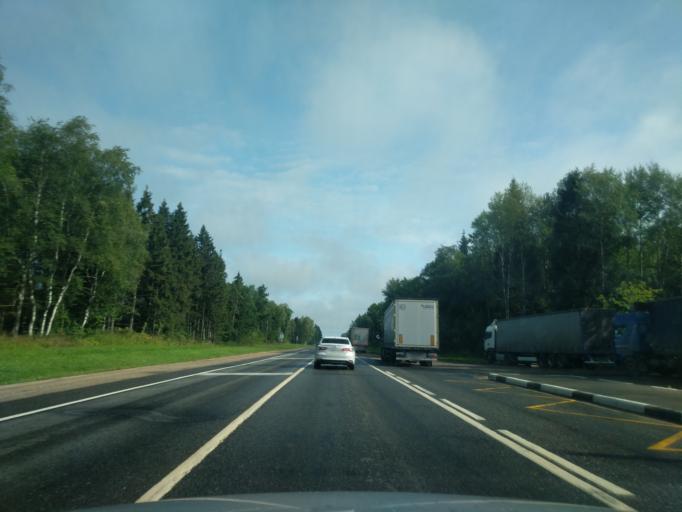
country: RU
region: Jaroslavl
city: Pereslavl'-Zalesskiy
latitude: 56.7929
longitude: 38.8888
